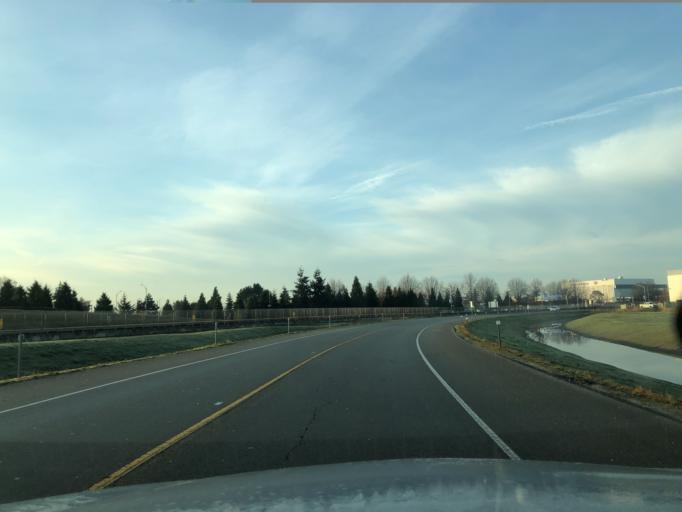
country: CA
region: British Columbia
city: Richmond
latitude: 49.1948
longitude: -123.1523
